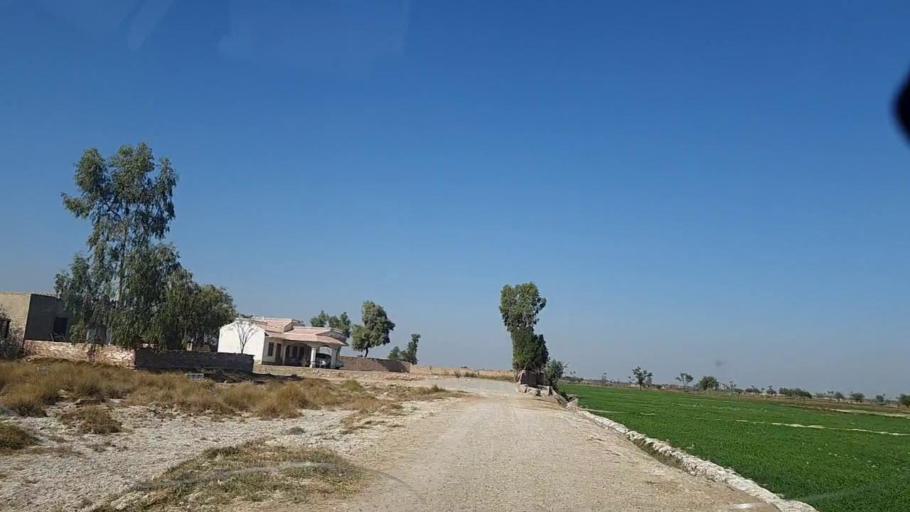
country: PK
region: Sindh
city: Khanpur
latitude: 27.8497
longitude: 69.3919
